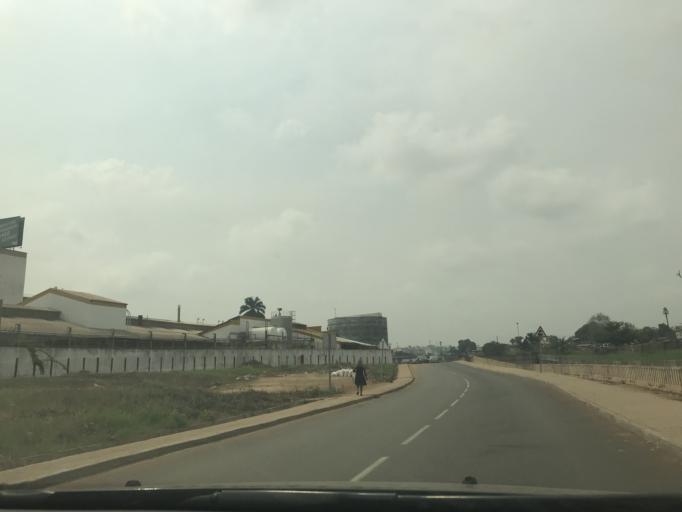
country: CM
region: Centre
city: Yaounde
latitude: 3.8416
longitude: 11.5135
